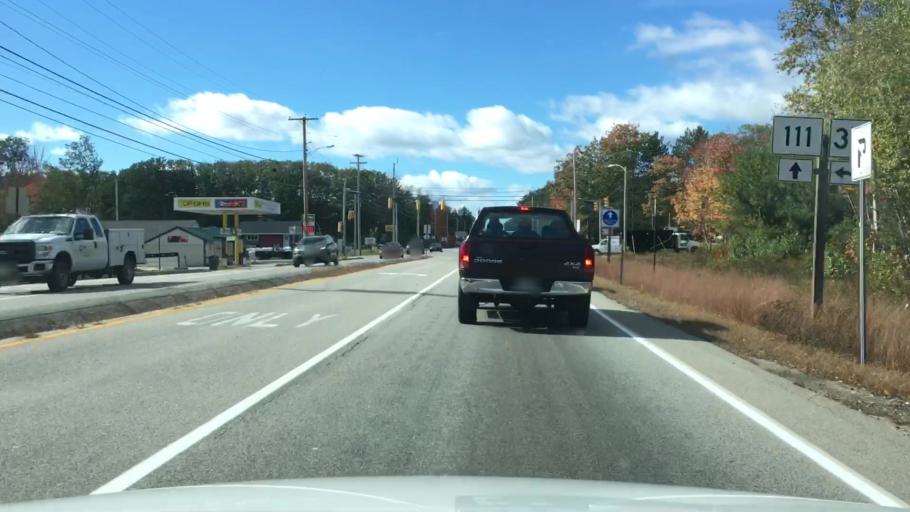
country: US
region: Maine
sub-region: York County
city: West Kennebunk
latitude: 43.4795
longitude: -70.6033
